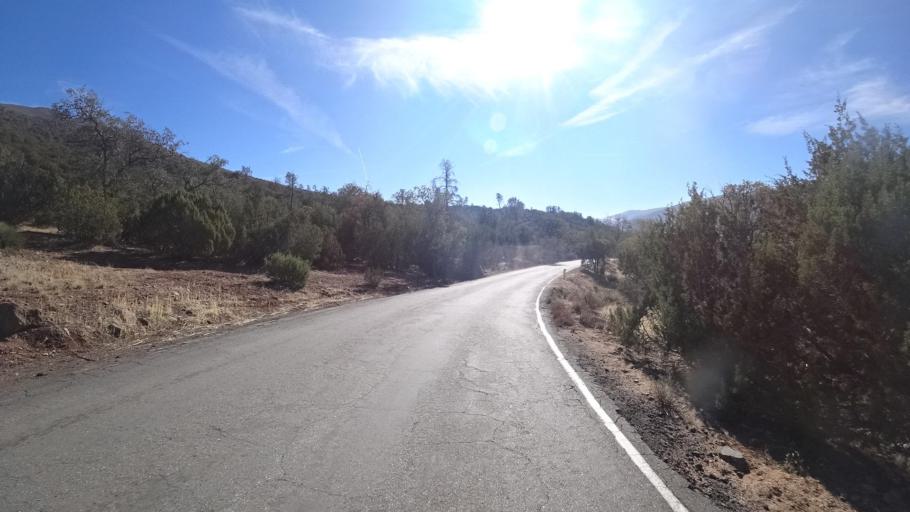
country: US
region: California
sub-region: Kern County
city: Bodfish
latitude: 35.5627
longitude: -118.5041
